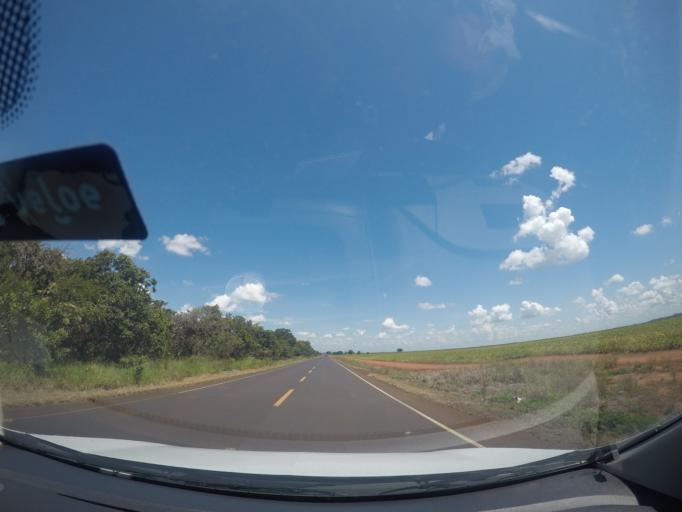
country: BR
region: Minas Gerais
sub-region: Frutal
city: Frutal
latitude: -19.7089
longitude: -48.7698
